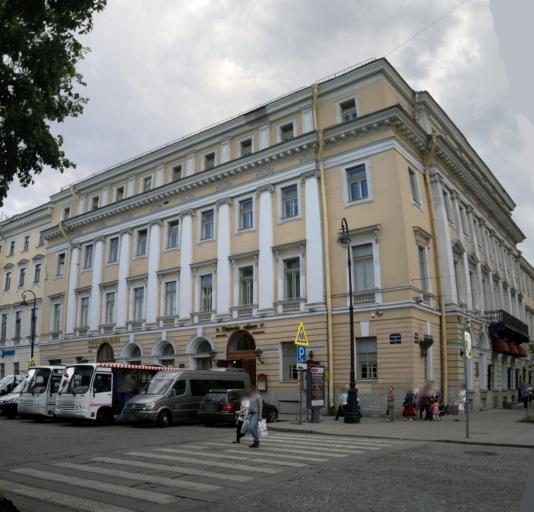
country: RU
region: St.-Petersburg
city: Saint Petersburg
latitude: 59.9367
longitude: 30.3315
